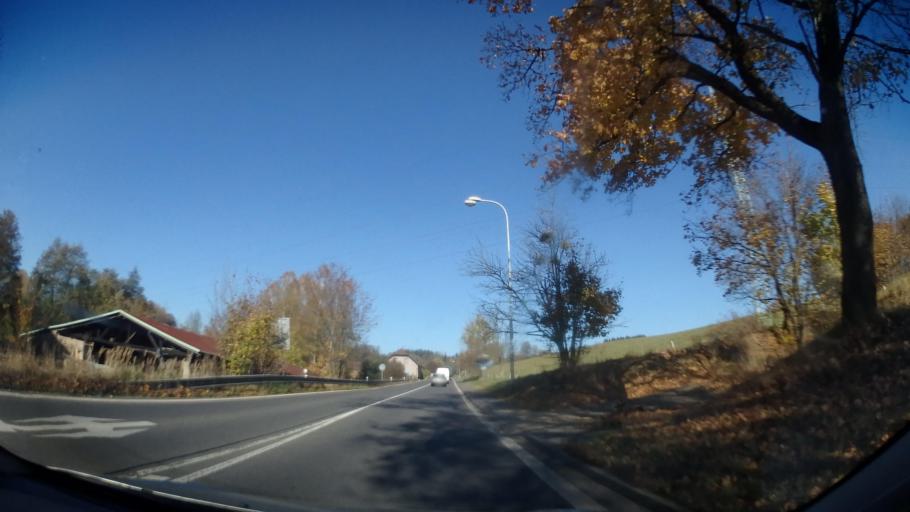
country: CZ
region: Pardubicky
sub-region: Okres Chrudim
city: Nasavrky
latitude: 49.7907
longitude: 15.8122
